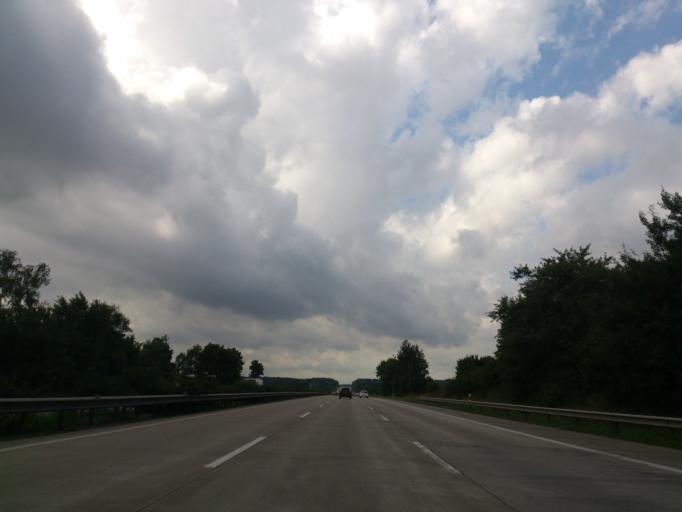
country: DE
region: Lower Saxony
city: Bispingen
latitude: 53.1002
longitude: 9.9766
